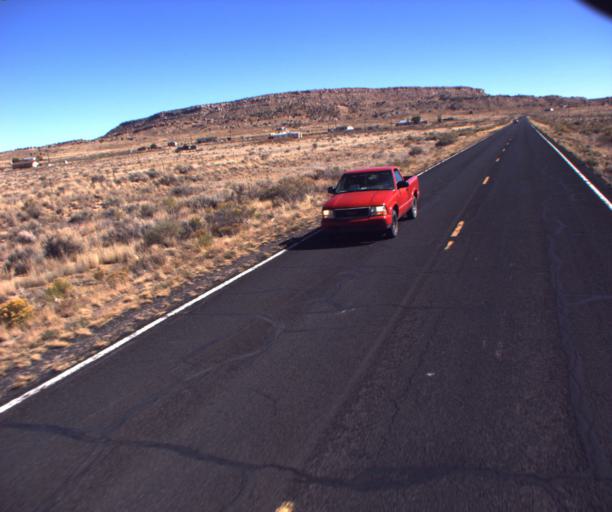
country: US
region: Arizona
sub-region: Navajo County
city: First Mesa
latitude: 35.8401
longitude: -110.3137
